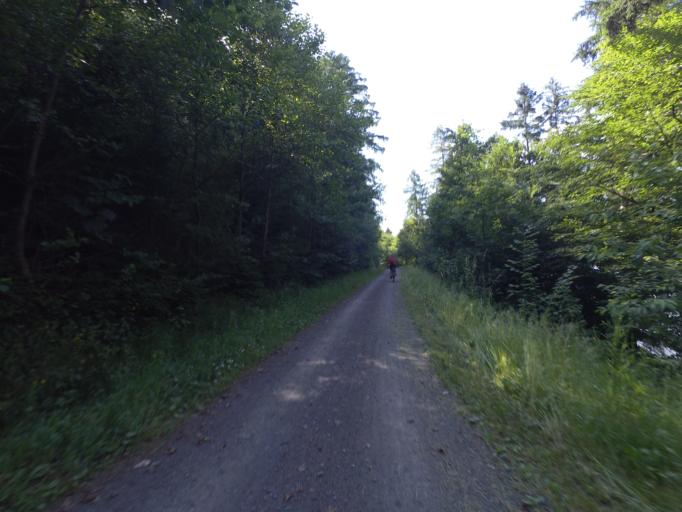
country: AT
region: Carinthia
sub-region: Politischer Bezirk Spittal an der Drau
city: Millstatt
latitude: 46.7867
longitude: 13.5880
